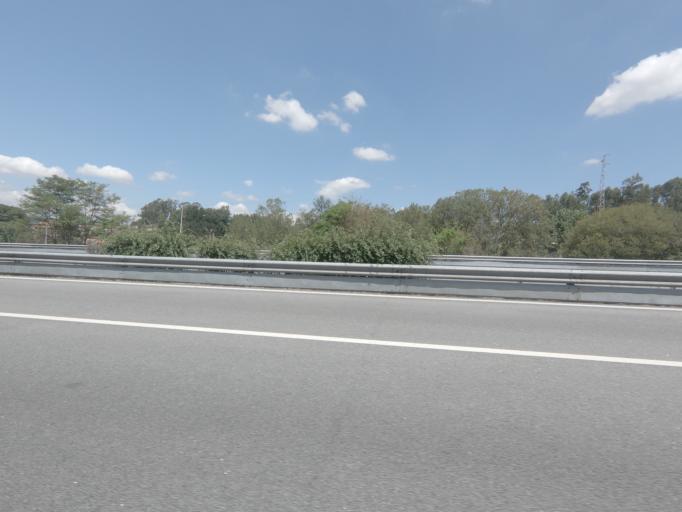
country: PT
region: Porto
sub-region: Paredes
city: Paredes
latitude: 41.2019
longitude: -8.3116
